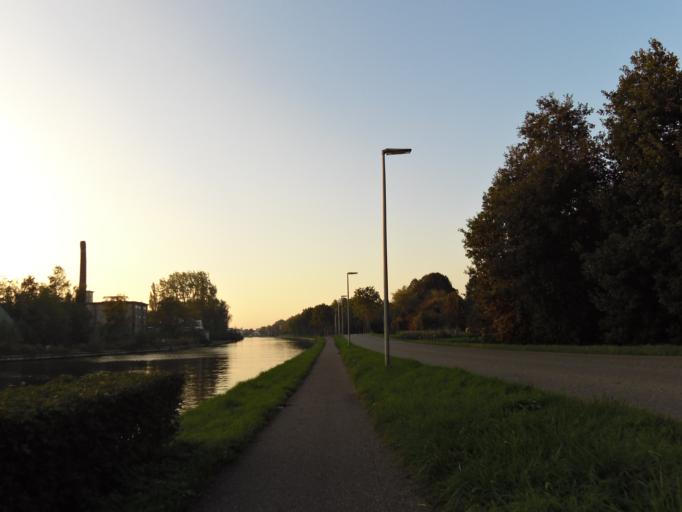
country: NL
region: South Holland
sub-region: Gemeente Leiderdorp
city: Leiderdorp
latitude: 52.1354
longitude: 4.5557
